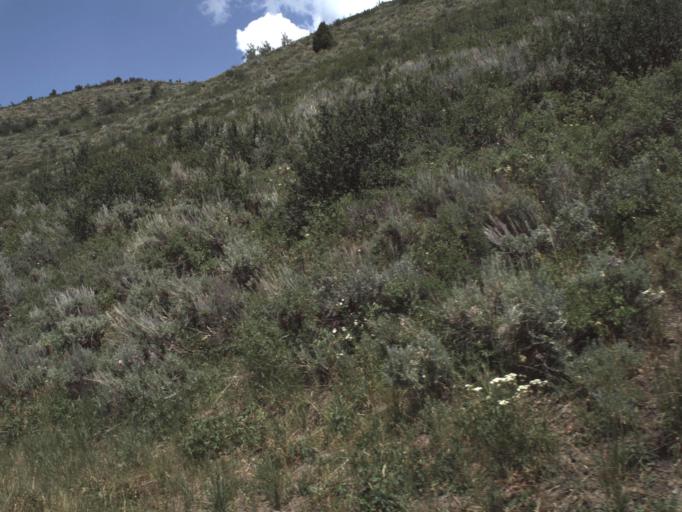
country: US
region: Utah
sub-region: Weber County
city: Wolf Creek
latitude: 41.3759
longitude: -111.5898
